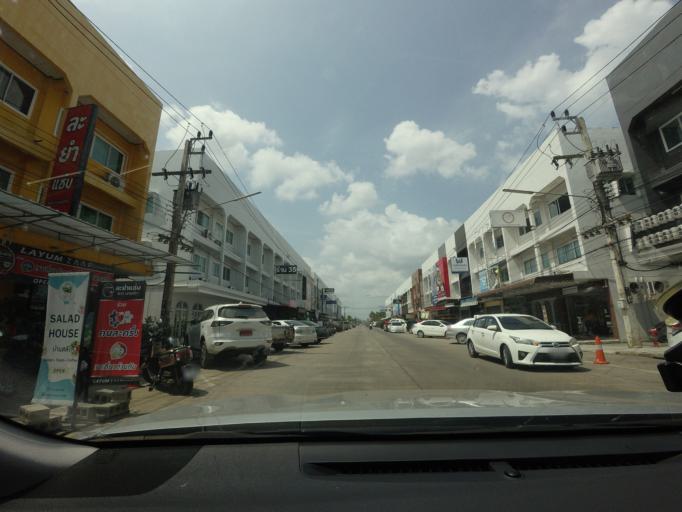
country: TH
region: Nakhon Si Thammarat
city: Nakhon Si Thammarat
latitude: 8.4288
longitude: 99.9806
